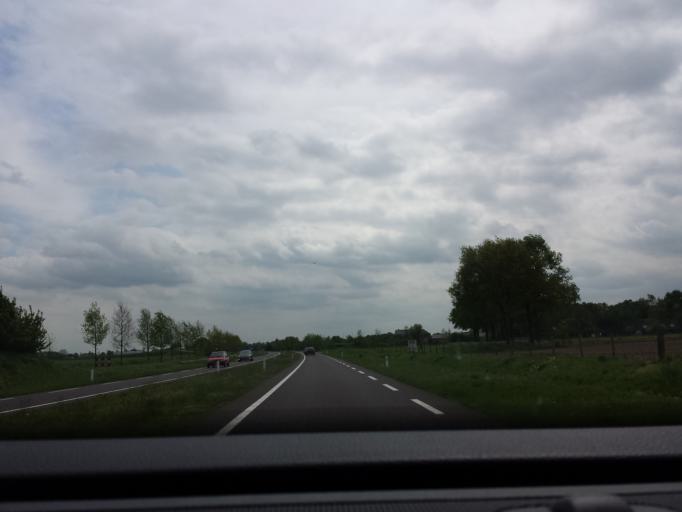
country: NL
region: Gelderland
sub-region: Gemeente Montferland
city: s-Heerenberg
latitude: 51.9094
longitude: 6.2672
